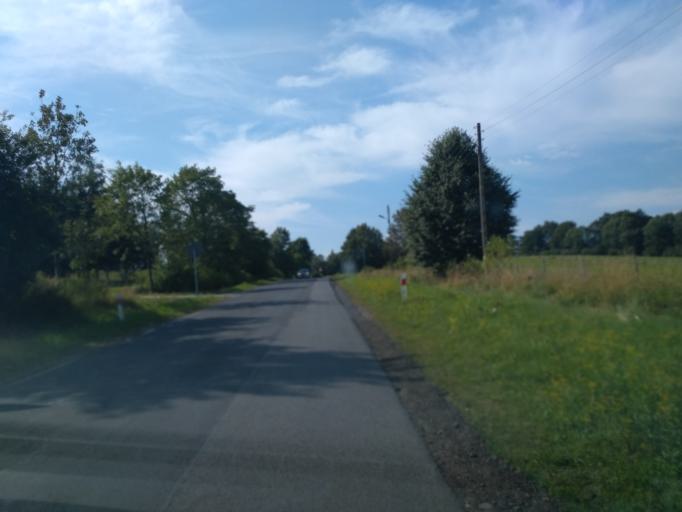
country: PL
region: Subcarpathian Voivodeship
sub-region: Powiat bieszczadzki
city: Lutowiska
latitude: 49.2569
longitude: 22.6867
